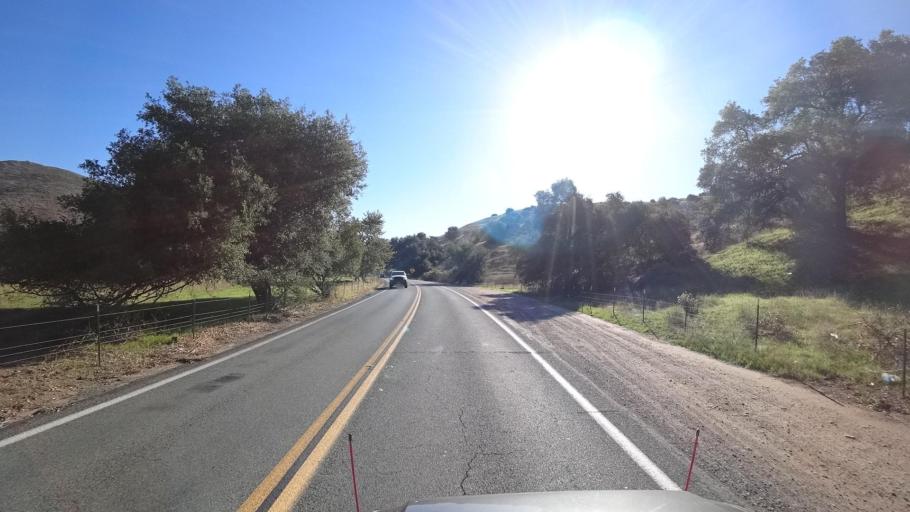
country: US
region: California
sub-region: San Diego County
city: Jamul
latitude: 32.6677
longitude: -116.8261
